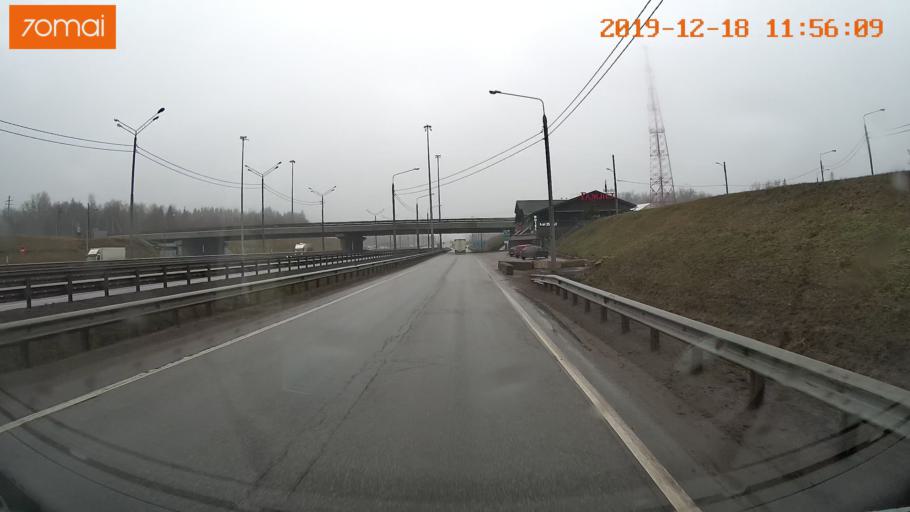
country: RU
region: Moskovskaya
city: Yershovo
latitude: 55.8235
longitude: 36.9202
